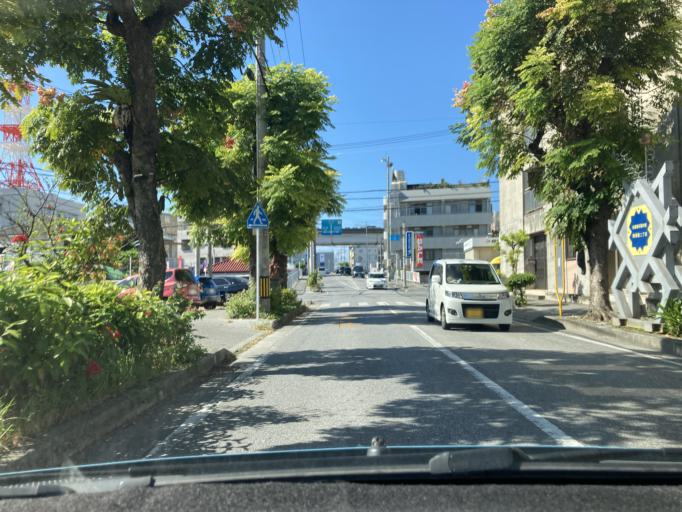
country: JP
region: Okinawa
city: Naha-shi
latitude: 26.2423
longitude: 127.6930
